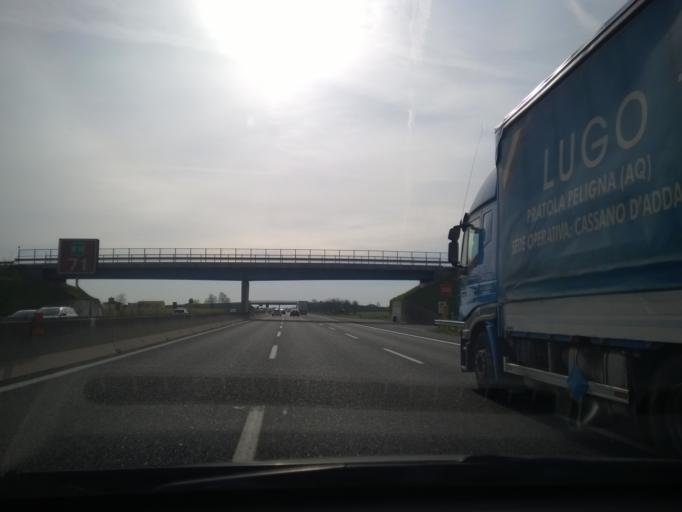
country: IT
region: Emilia-Romagna
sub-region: Forli-Cesena
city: Forlimpopoli
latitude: 44.2439
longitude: 12.1188
